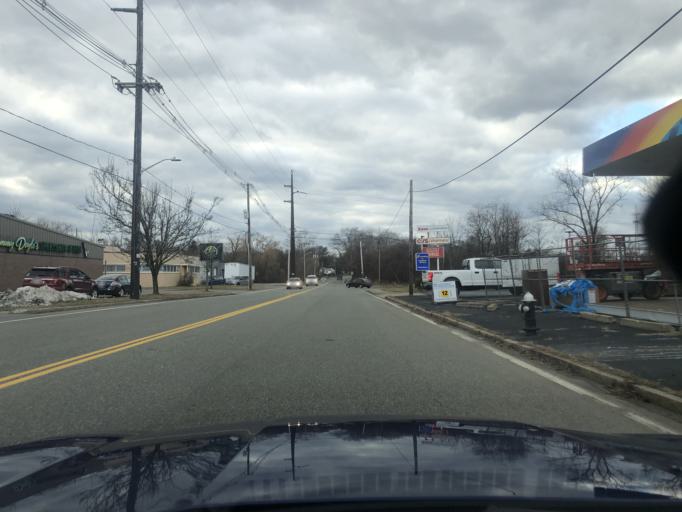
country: US
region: Massachusetts
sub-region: Plymouth County
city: Brockton
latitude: 42.0961
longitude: -71.0095
